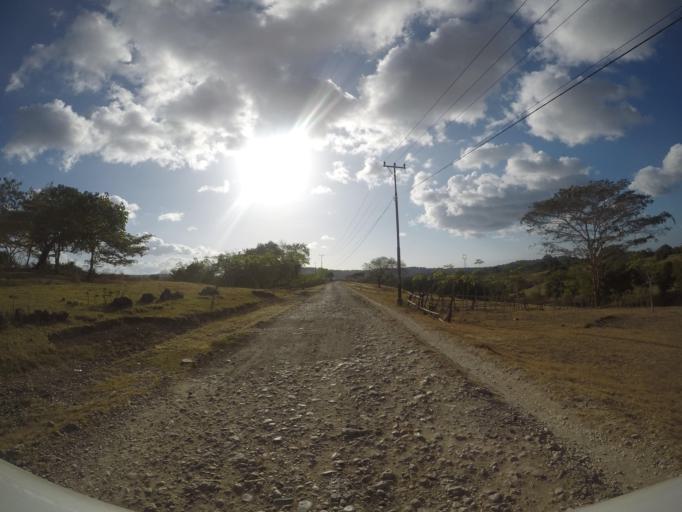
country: TL
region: Lautem
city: Lospalos
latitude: -8.4292
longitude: 126.8416
